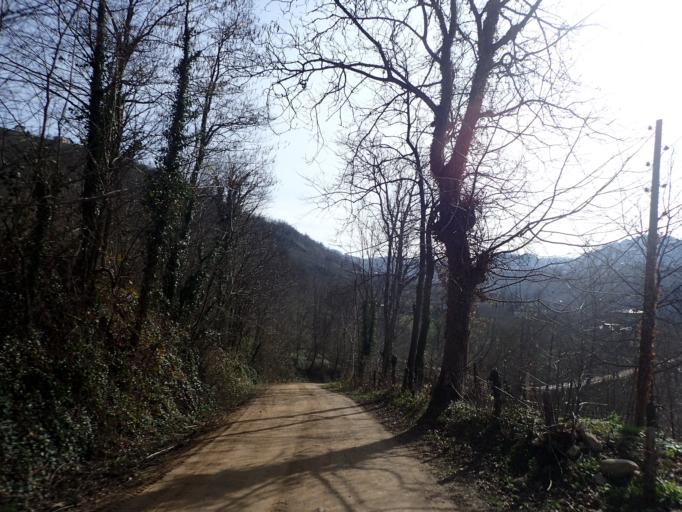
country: TR
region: Ordu
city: Camas
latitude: 40.9415
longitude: 37.5141
